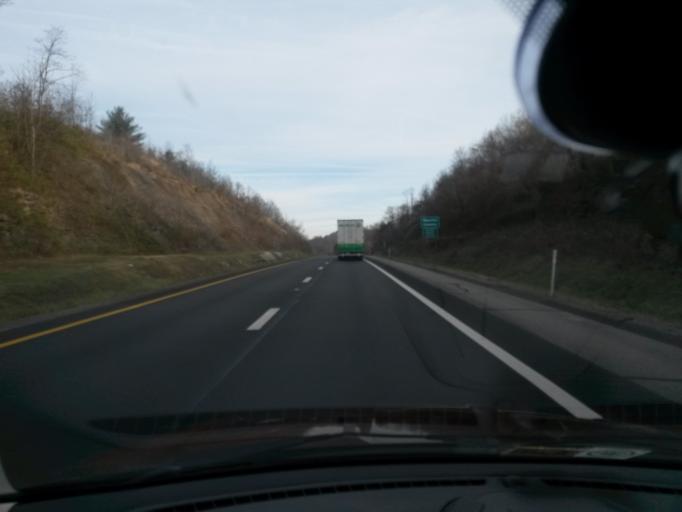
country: US
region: West Virginia
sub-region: Raleigh County
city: Bradley
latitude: 37.8866
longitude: -81.2665
